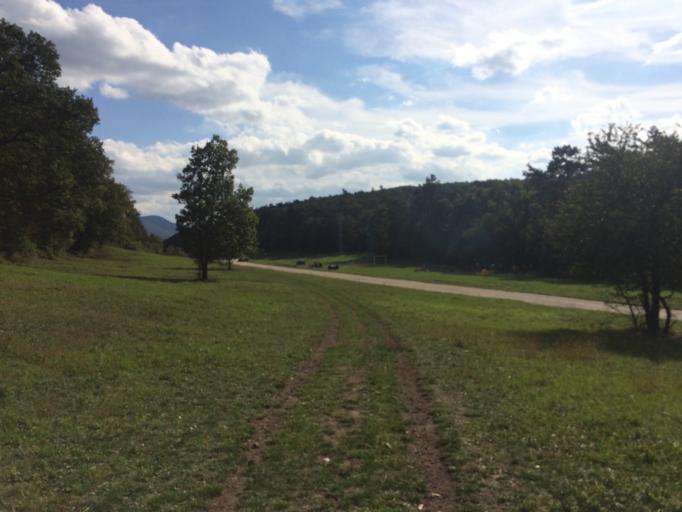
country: HU
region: Pest
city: Nagymaros
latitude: 47.8000
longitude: 18.9433
